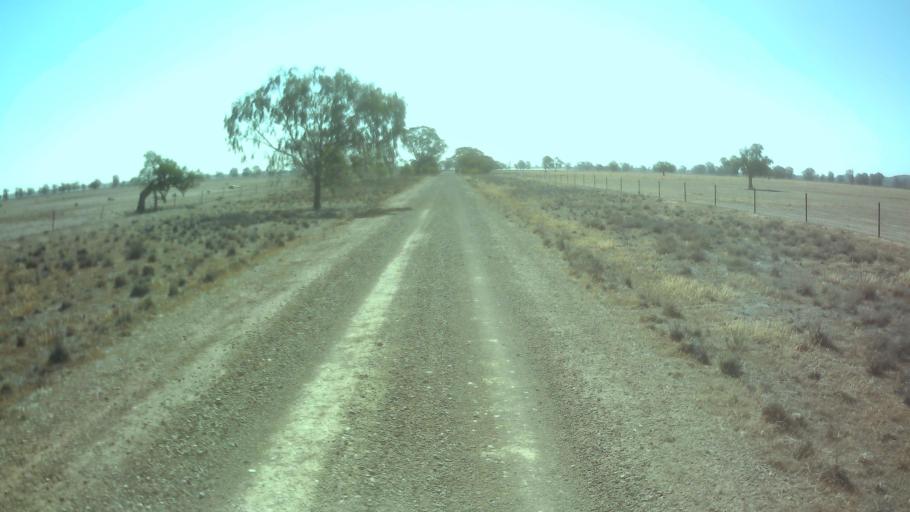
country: AU
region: New South Wales
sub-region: Weddin
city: Grenfell
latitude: -33.7591
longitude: 147.7023
